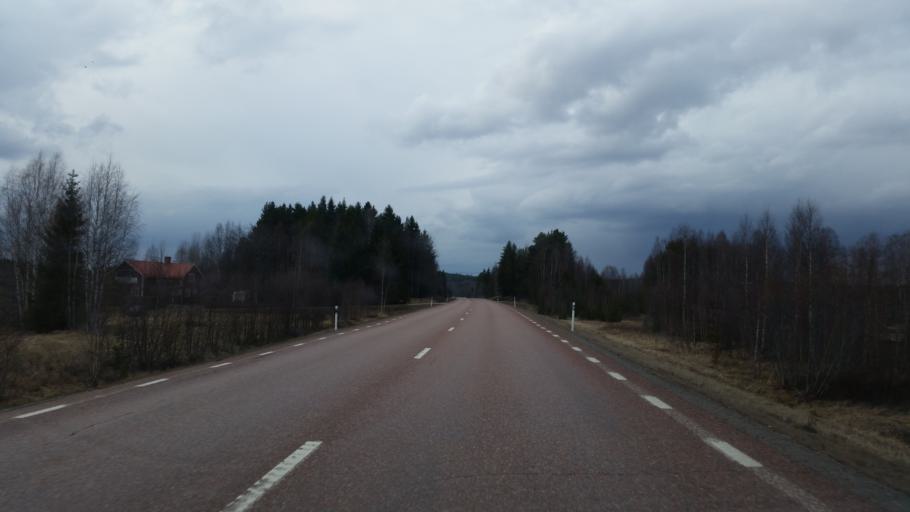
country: SE
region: Gaevleborg
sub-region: Ljusdals Kommun
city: Jaervsoe
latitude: 61.7791
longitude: 16.1438
